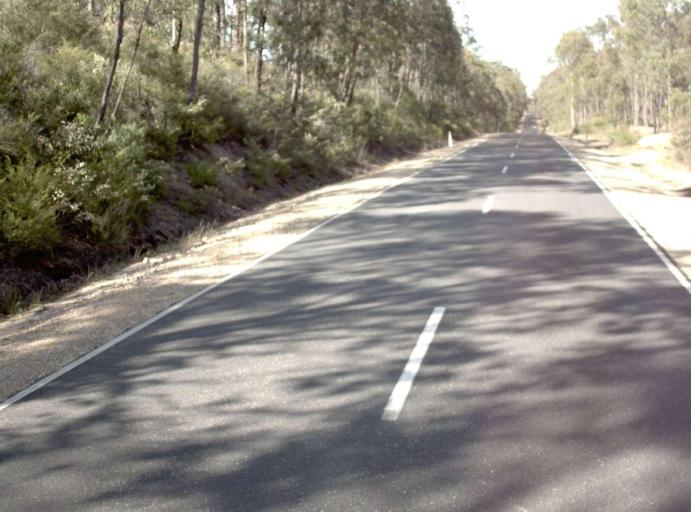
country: AU
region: Victoria
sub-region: East Gippsland
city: Lakes Entrance
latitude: -37.6541
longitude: 148.0948
